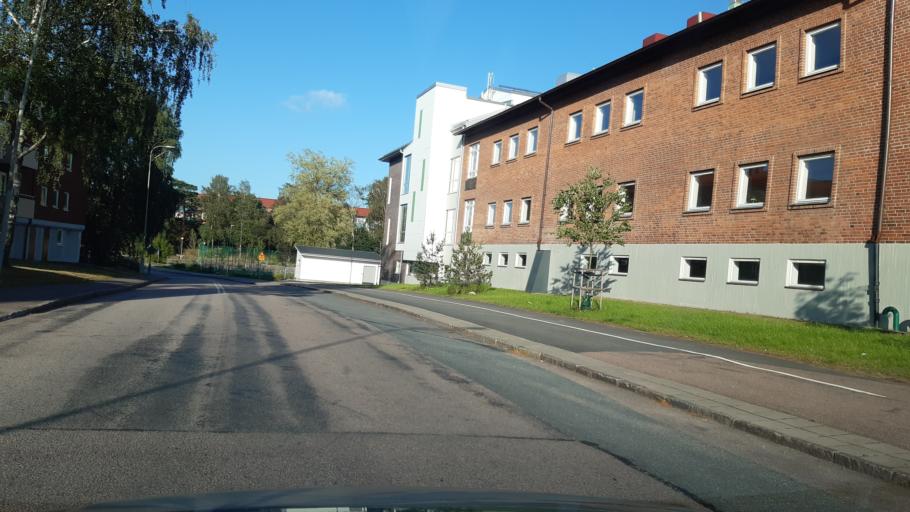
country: SE
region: Vaestra Goetaland
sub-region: Goteborg
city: Eriksbo
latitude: 57.7146
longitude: 12.0478
